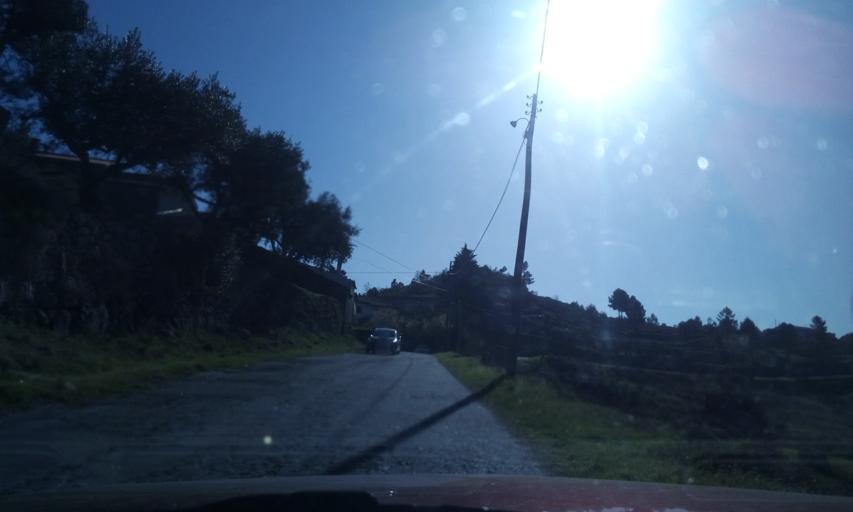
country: PT
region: Guarda
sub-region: Celorico da Beira
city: Celorico da Beira
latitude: 40.6867
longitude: -7.3994
